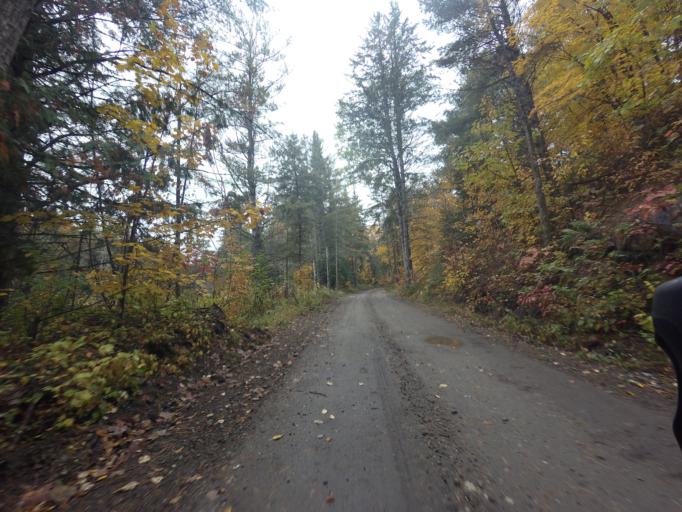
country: CA
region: Ontario
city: Renfrew
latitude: 45.1670
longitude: -76.6809
